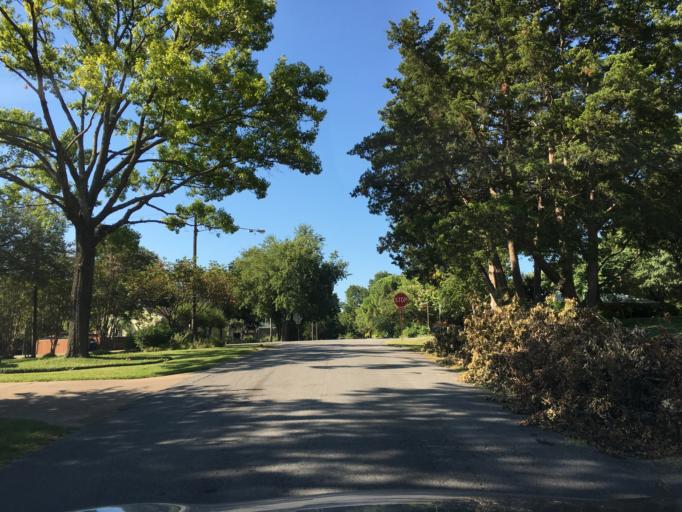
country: US
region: Texas
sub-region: Dallas County
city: Garland
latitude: 32.8619
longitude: -96.7057
